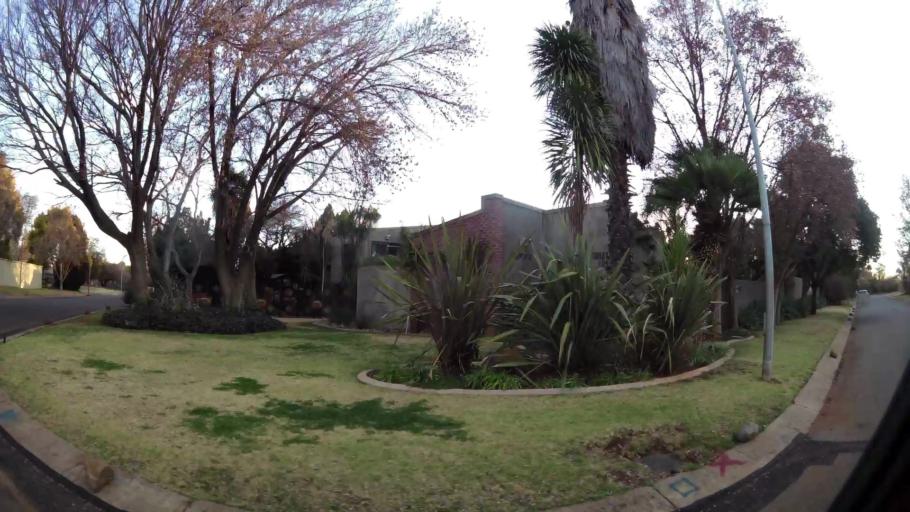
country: ZA
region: North-West
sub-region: Dr Kenneth Kaunda District Municipality
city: Potchefstroom
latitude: -26.6785
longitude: 27.1095
